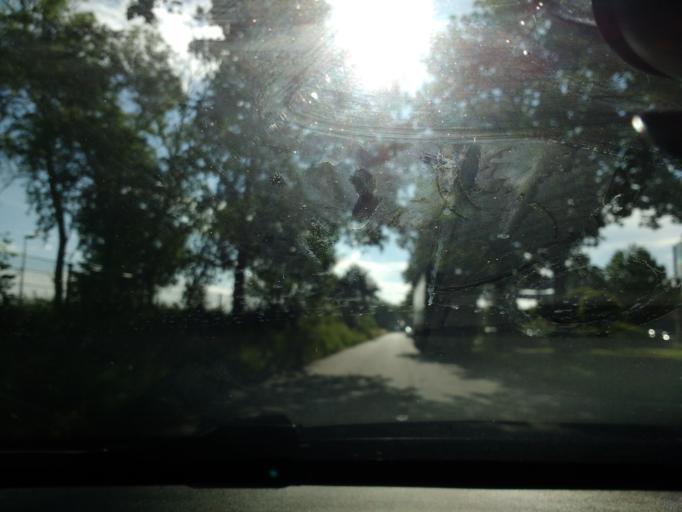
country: NL
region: Utrecht
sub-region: Gemeente Veenendaal
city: Veenendaal
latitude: 52.0420
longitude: 5.5413
